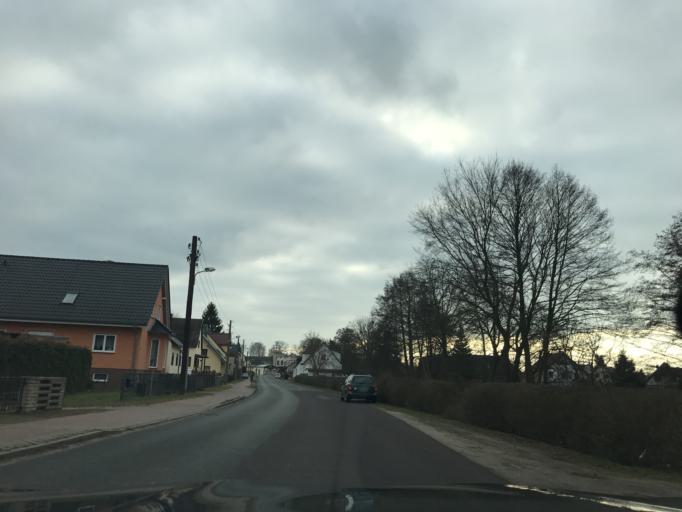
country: DE
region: Brandenburg
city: Brandenburg an der Havel
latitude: 52.3710
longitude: 12.5467
